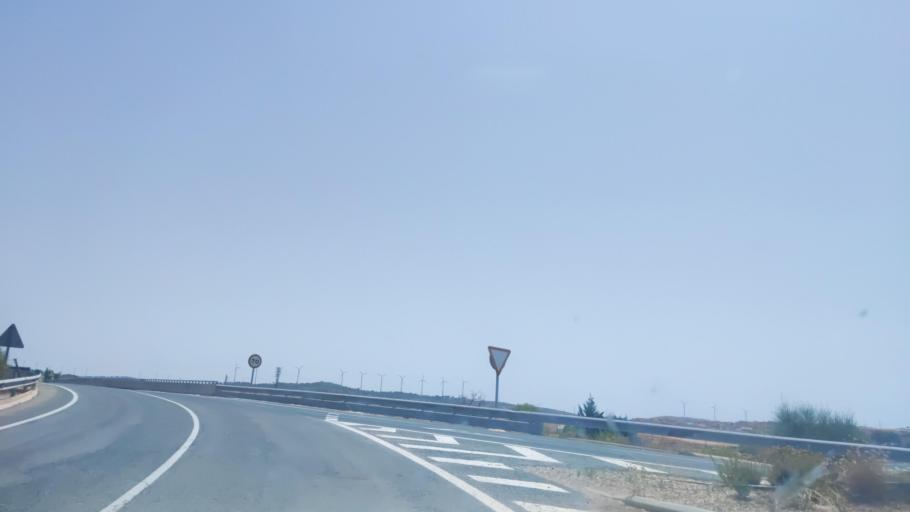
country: ES
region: Castille-La Mancha
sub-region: Provincia de Albacete
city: Pozo-Canada
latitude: 38.8105
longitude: -1.7422
